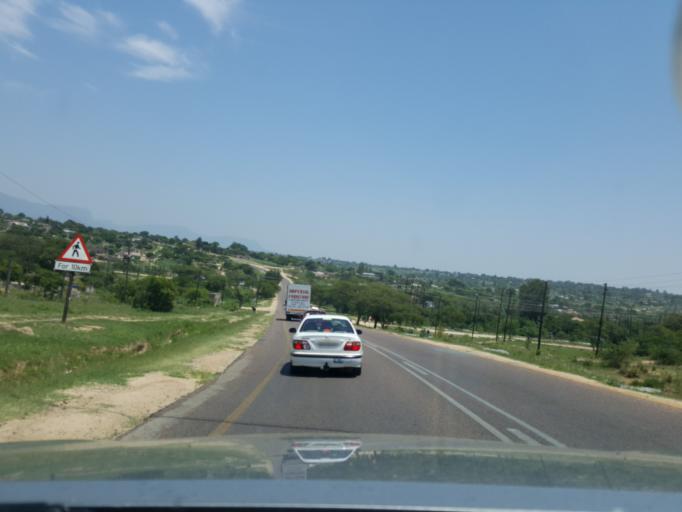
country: ZA
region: Limpopo
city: Thulamahashi
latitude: -24.7915
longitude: 31.0818
